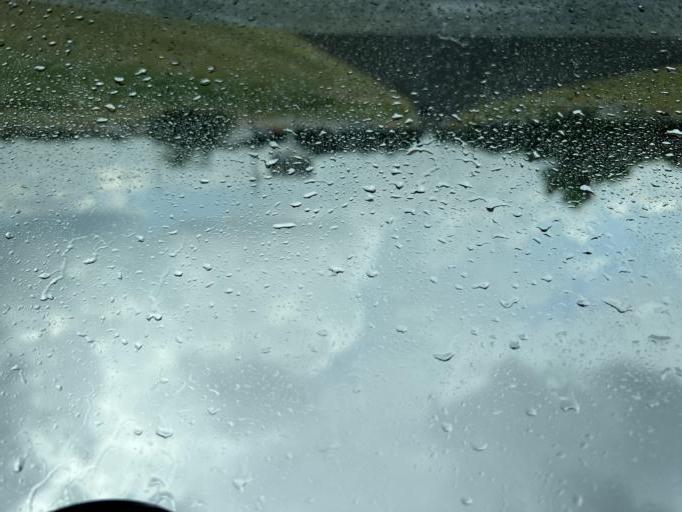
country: US
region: Texas
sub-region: Wise County
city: Decatur
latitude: 33.1554
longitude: -97.6329
